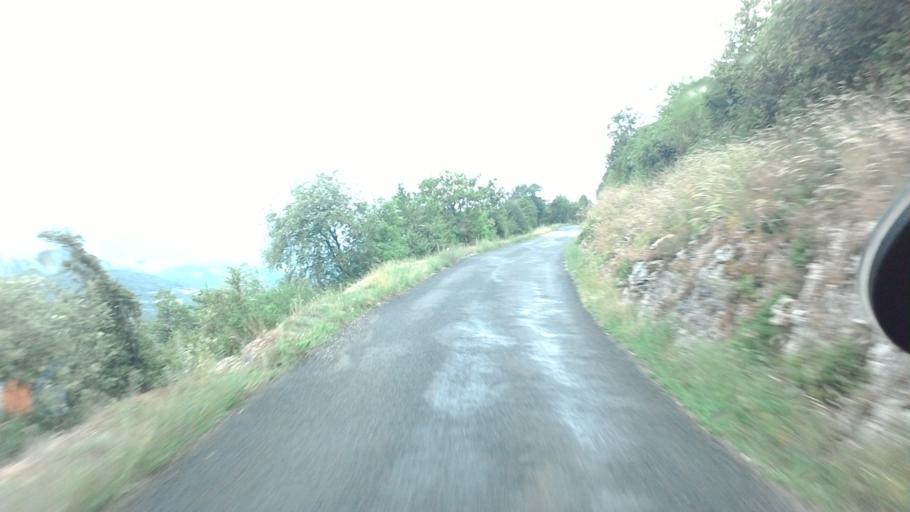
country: FR
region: Rhone-Alpes
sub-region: Departement de l'Ain
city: Belley
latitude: 45.7481
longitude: 5.5953
